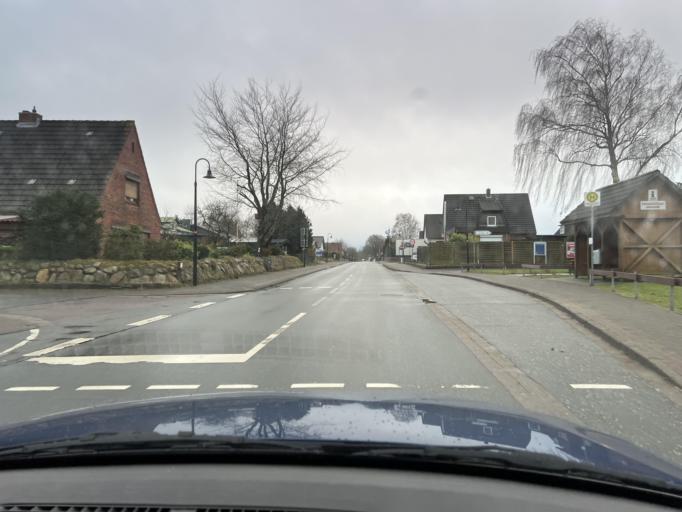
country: DE
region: Schleswig-Holstein
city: Lohe-Rickelshof
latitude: 54.2097
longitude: 9.0745
